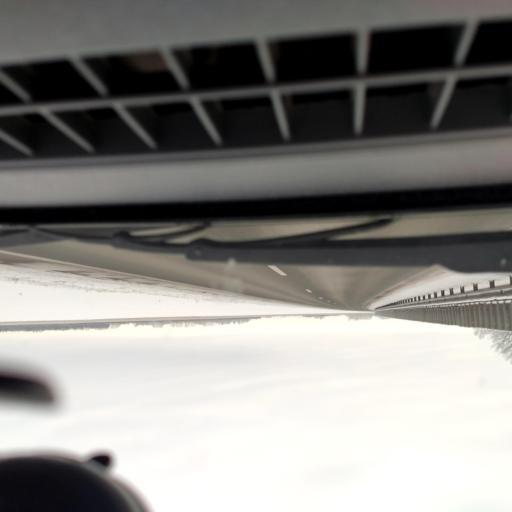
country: RU
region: Bashkortostan
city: Kushnarenkovo
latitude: 55.0673
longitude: 55.3440
